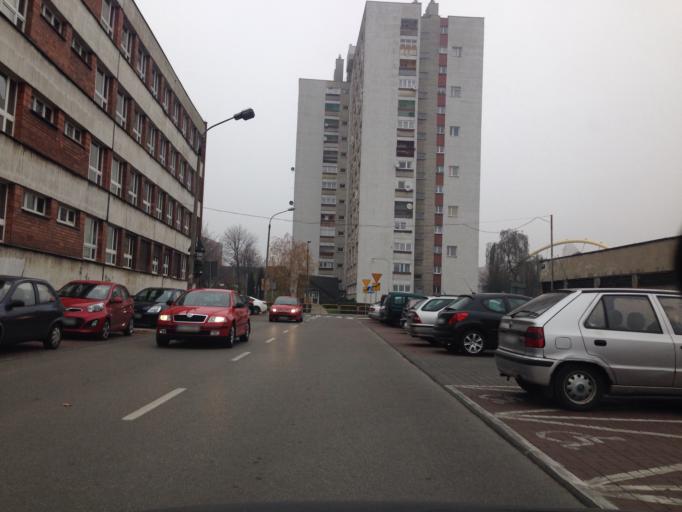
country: PL
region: Silesian Voivodeship
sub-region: Katowice
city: Katowice
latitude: 50.2615
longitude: 19.0292
